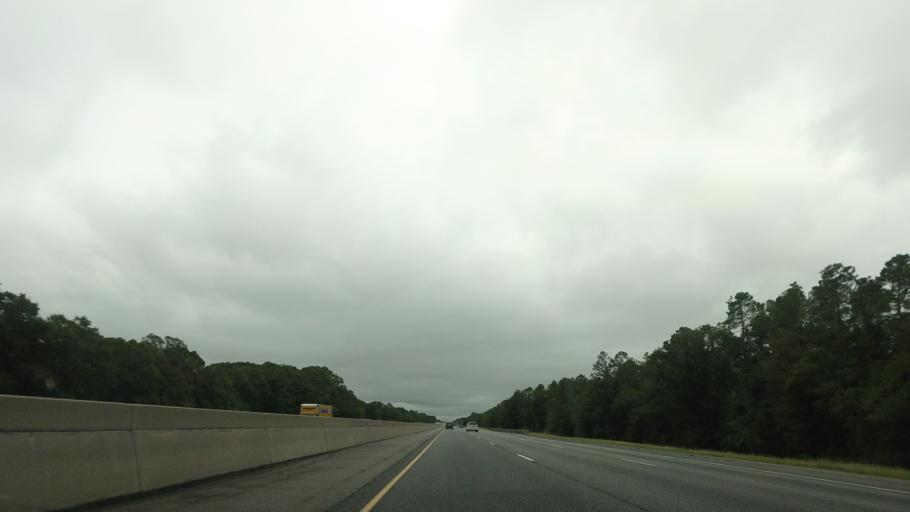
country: US
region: Georgia
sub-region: Turner County
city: Ashburn
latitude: 31.7730
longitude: -83.6803
